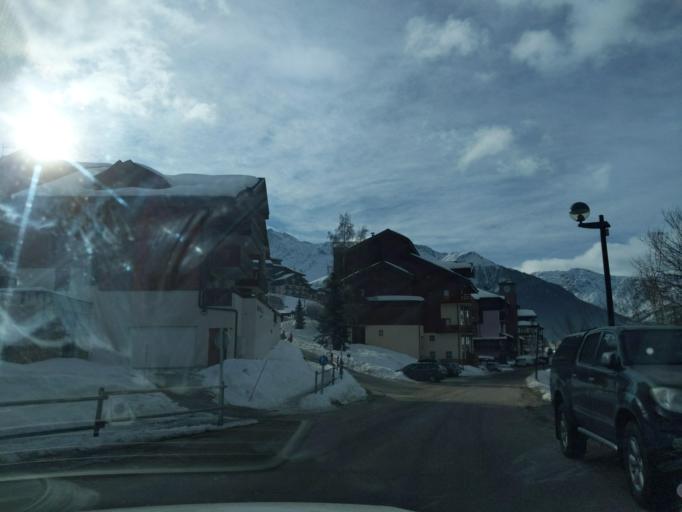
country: FR
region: Rhone-Alpes
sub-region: Departement de la Savoie
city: Bourg-Saint-Maurice
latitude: 45.5579
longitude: 6.7624
